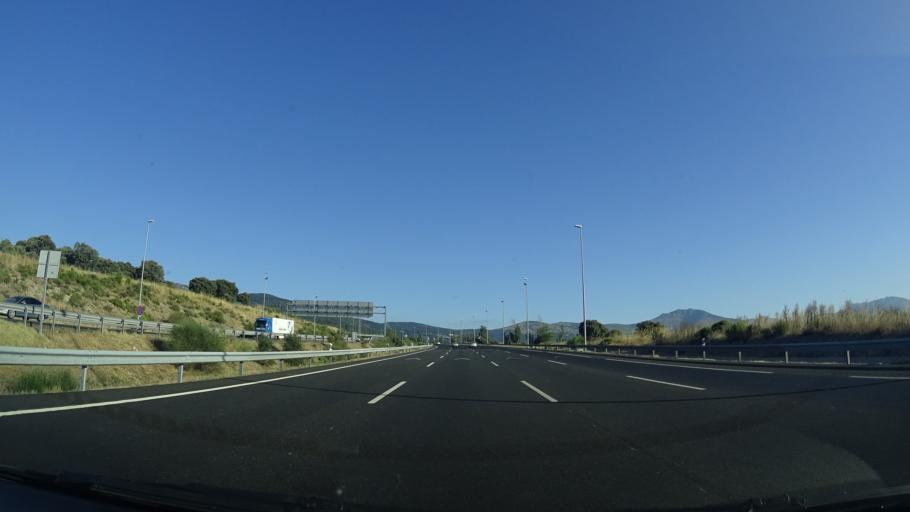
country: ES
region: Madrid
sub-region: Provincia de Madrid
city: Guadarrama
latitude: 40.6638
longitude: -4.1001
